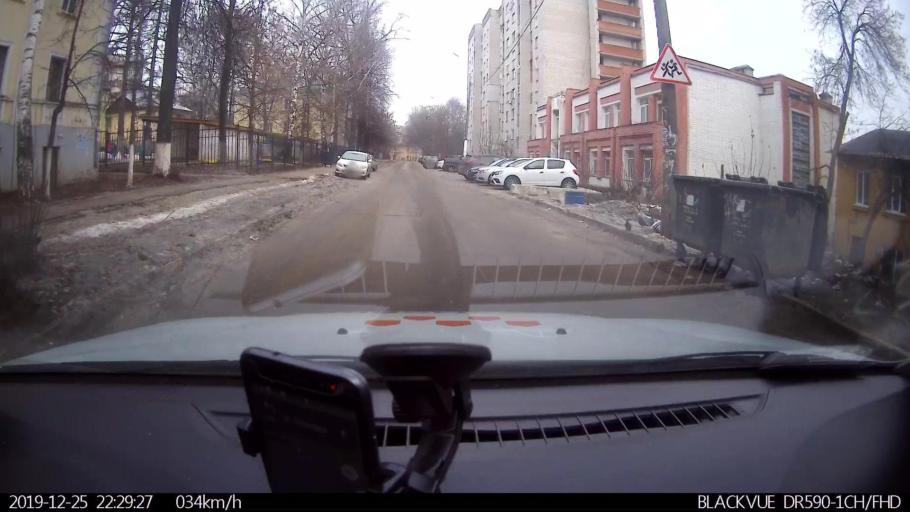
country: RU
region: Nizjnij Novgorod
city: Nizhniy Novgorod
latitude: 56.2675
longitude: 43.9845
